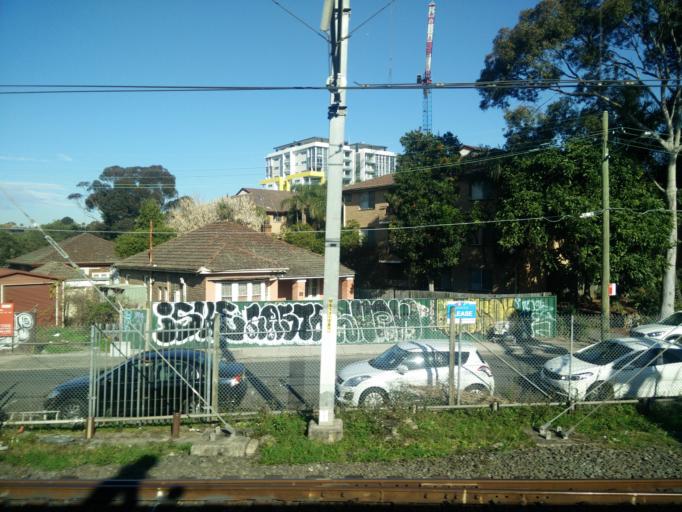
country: AU
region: New South Wales
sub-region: Strathfield
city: Homebush
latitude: -33.8734
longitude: 151.0963
